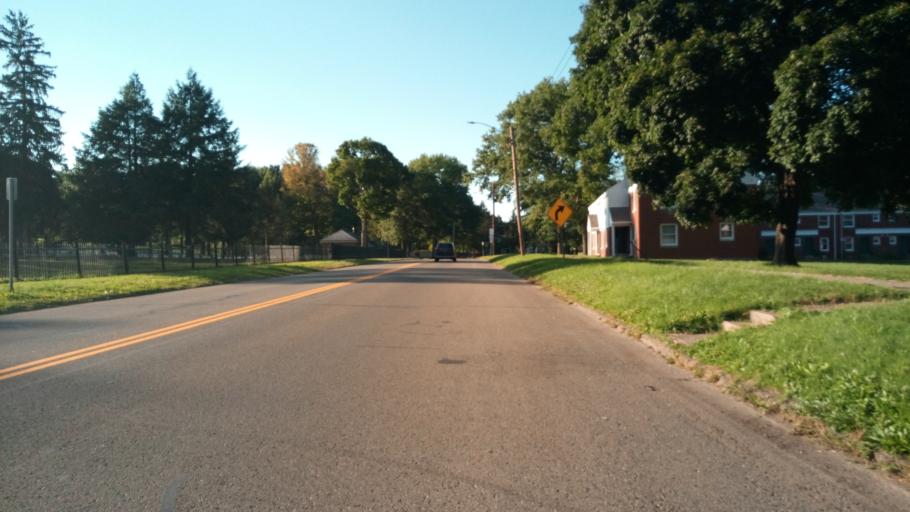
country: US
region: New York
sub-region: Chemung County
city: Elmira Heights
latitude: 42.1094
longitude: -76.8257
